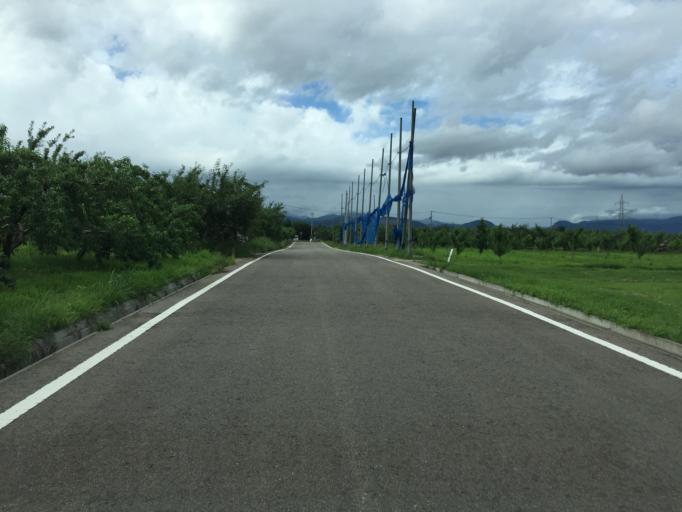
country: JP
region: Fukushima
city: Fukushima-shi
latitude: 37.7298
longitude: 140.4108
